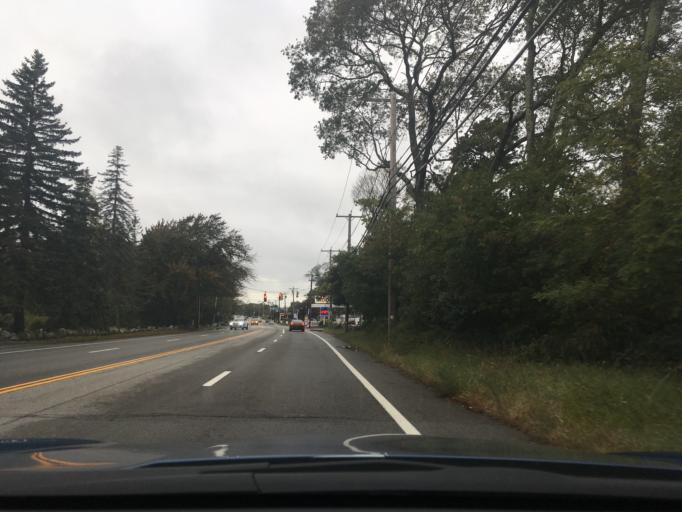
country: US
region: Rhode Island
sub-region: Kent County
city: East Greenwich
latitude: 41.6265
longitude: -71.4605
